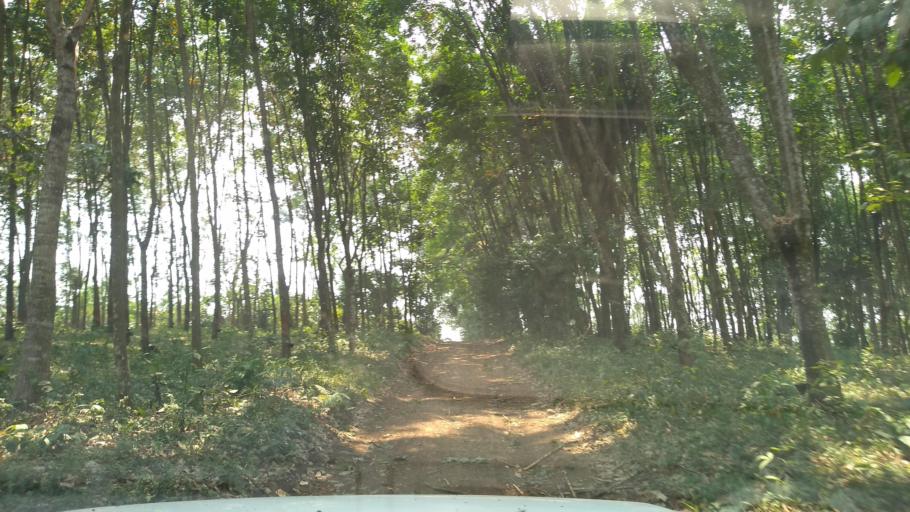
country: MX
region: Veracruz
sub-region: Tezonapa
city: Laguna Chica (Pueblo Nuevo)
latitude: 18.5330
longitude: -96.7603
